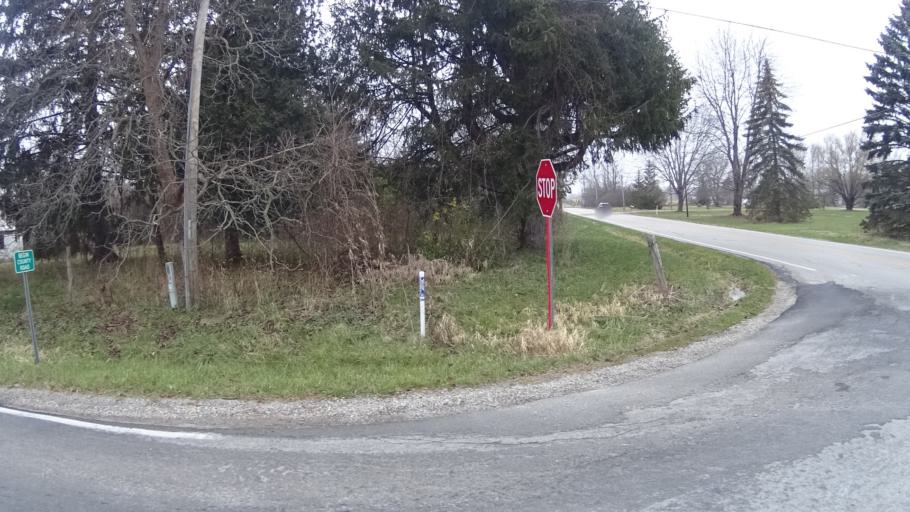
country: US
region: Ohio
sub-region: Lorain County
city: Oberlin
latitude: 41.2811
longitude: -82.1789
